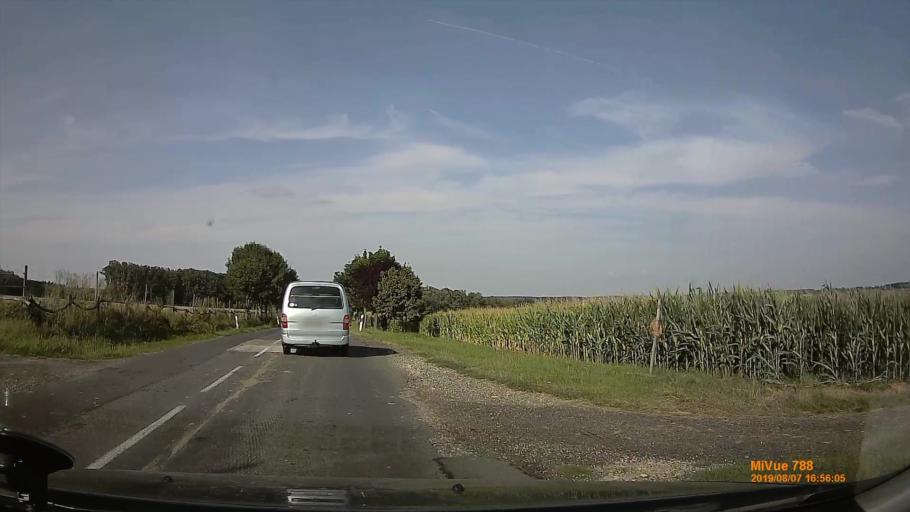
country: HU
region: Zala
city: Zalaegerszeg
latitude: 46.6915
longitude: 16.7397
